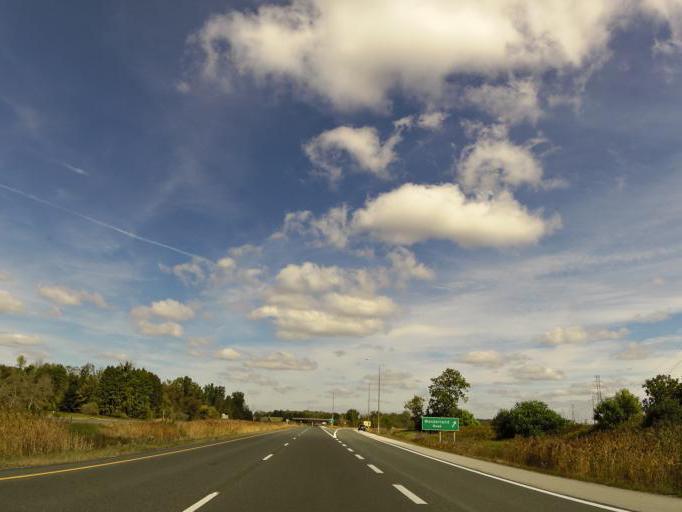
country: CA
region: Ontario
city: London
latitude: 42.8970
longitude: -81.2764
